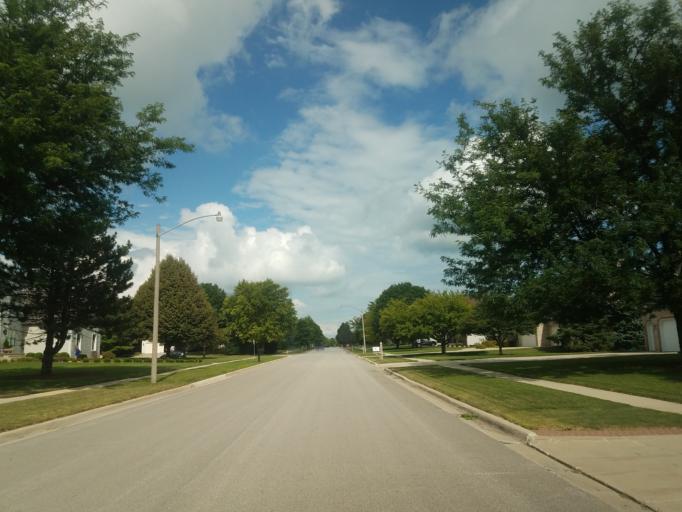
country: US
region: Illinois
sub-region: McLean County
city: Normal
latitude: 40.5077
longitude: -88.9169
